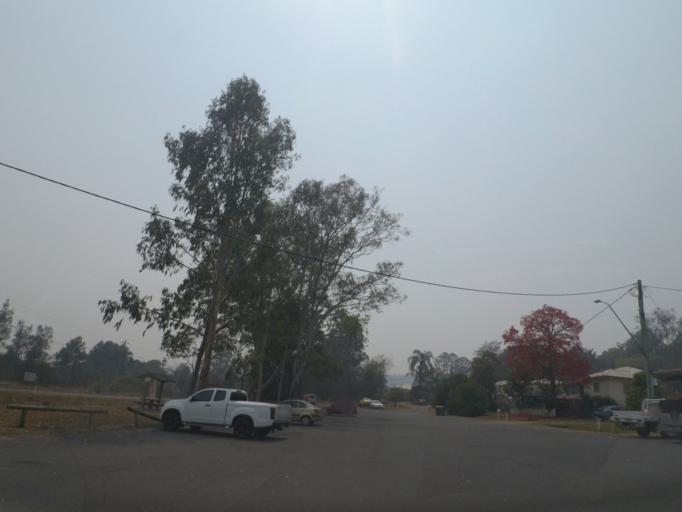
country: AU
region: New South Wales
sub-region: Clarence Valley
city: Maclean
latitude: -29.5651
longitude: 153.1437
